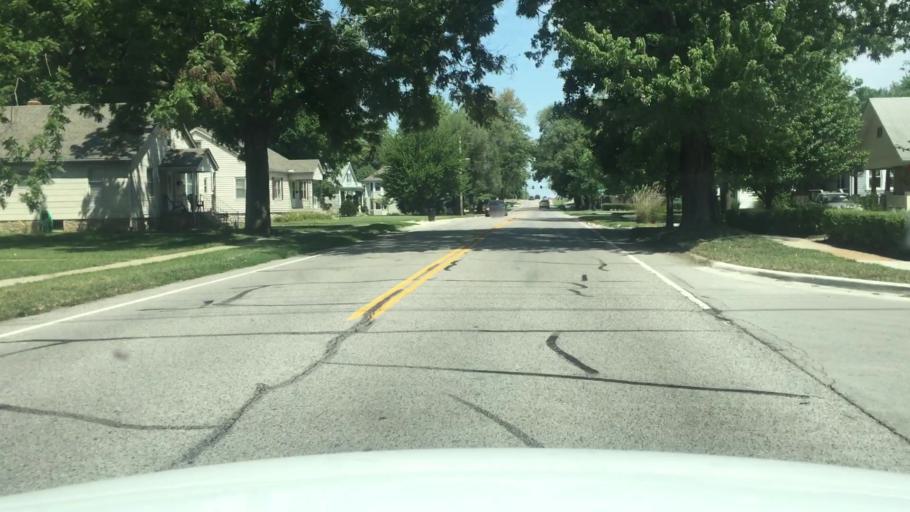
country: US
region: Missouri
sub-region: Jackson County
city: Lees Summit
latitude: 38.9214
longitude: -94.3800
